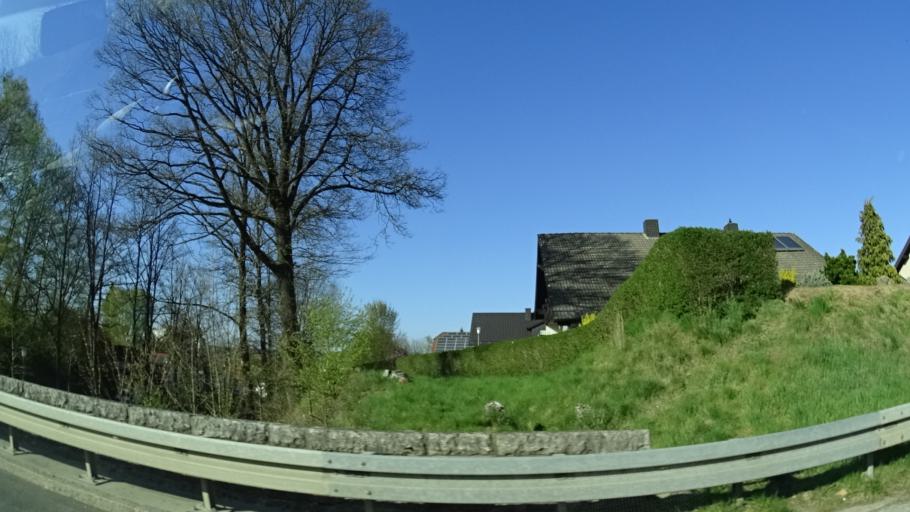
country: DE
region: Bavaria
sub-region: Upper Palatinate
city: Auerbach
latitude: 49.6852
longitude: 11.6325
